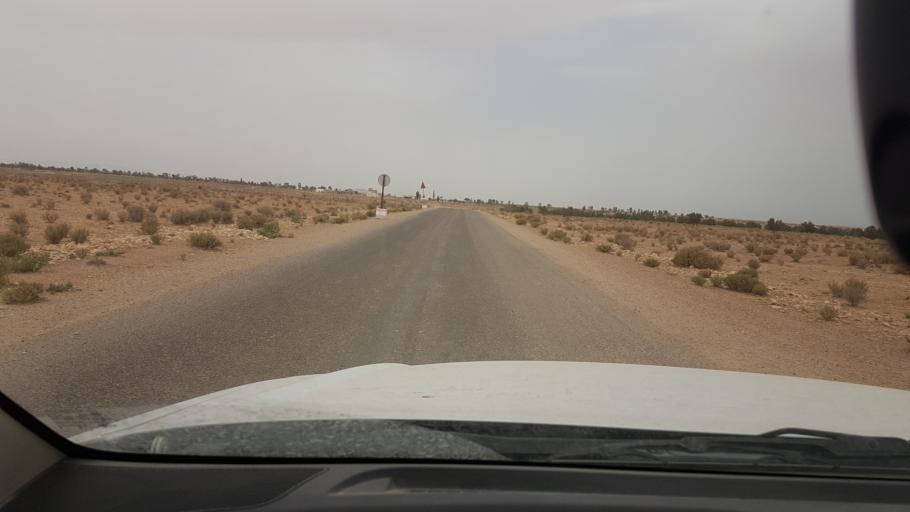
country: TN
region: Madanin
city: Medenine
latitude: 33.2870
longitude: 10.5951
